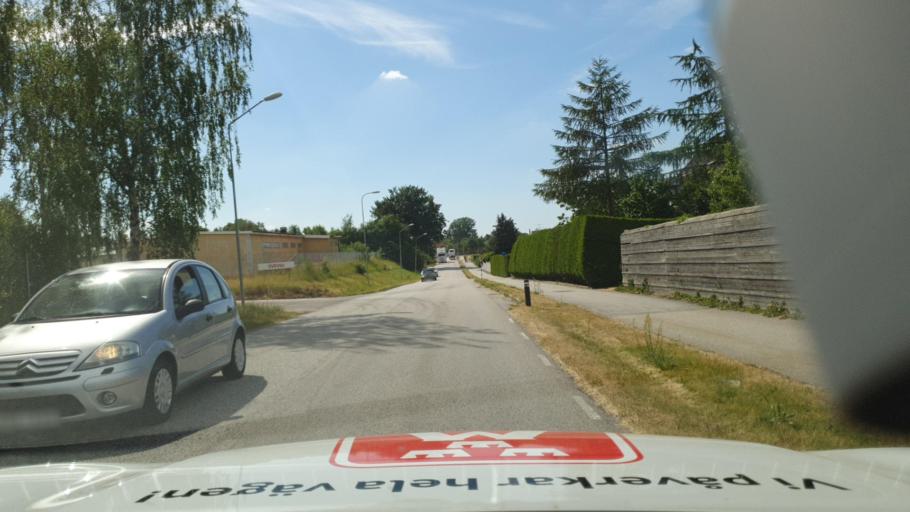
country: SE
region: Skane
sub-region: Sjobo Kommun
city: Sjoebo
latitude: 55.6284
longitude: 13.7178
